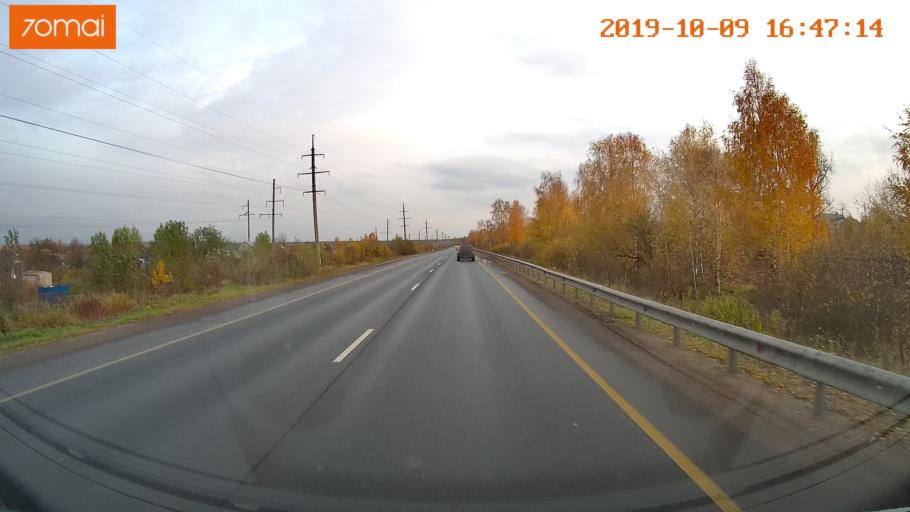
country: RU
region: Kostroma
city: Volgorechensk
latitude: 57.4384
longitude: 41.1749
